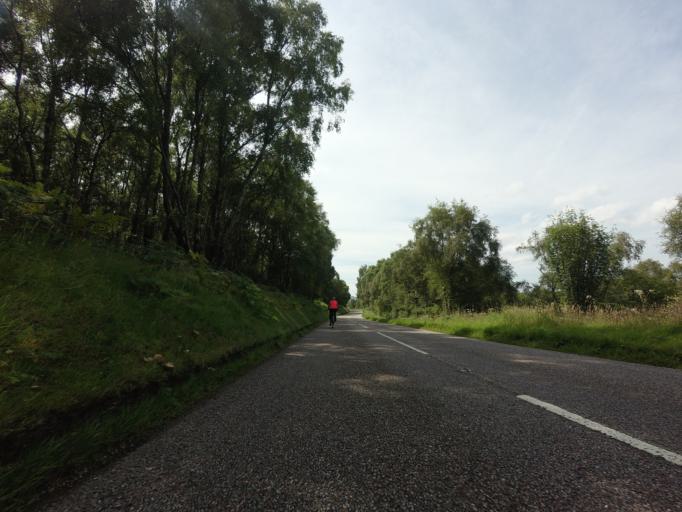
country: GB
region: Scotland
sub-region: Highland
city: Alness
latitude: 57.8575
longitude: -4.2427
